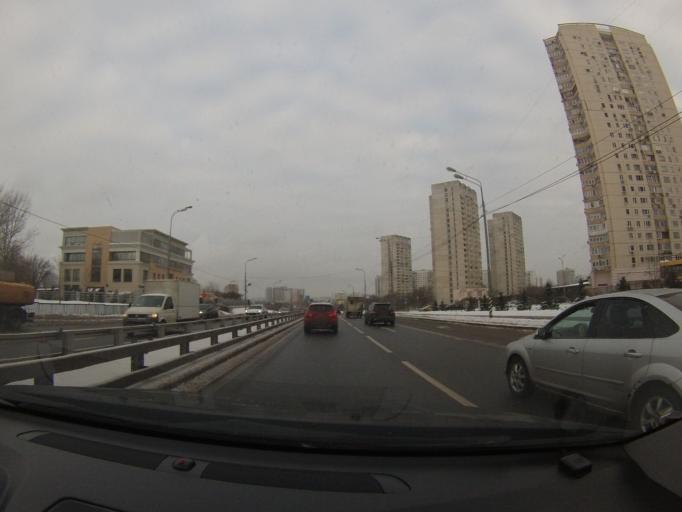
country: RU
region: Moscow
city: Nikol'skoye
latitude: 55.6803
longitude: 37.4820
